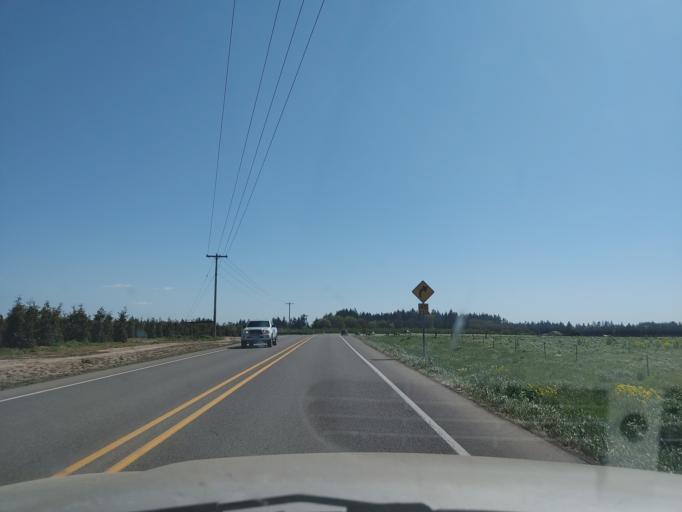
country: US
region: Oregon
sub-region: Yamhill County
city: Newberg
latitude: 45.2487
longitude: -122.9422
